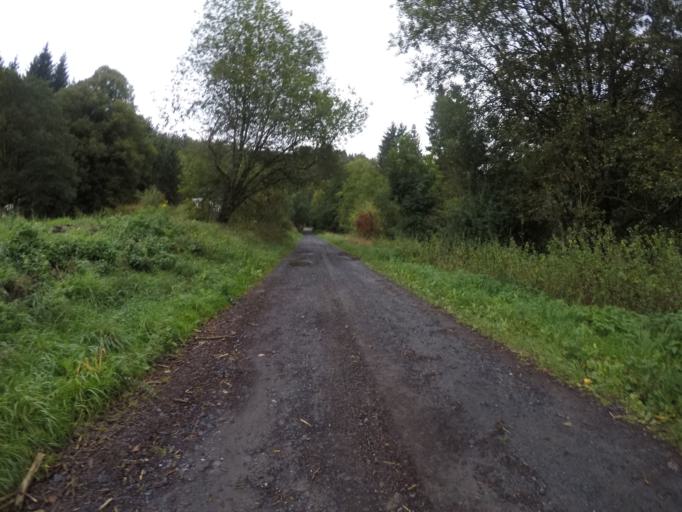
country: BE
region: Wallonia
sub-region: Province du Luxembourg
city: Fauvillers
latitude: 49.8556
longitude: 5.6990
